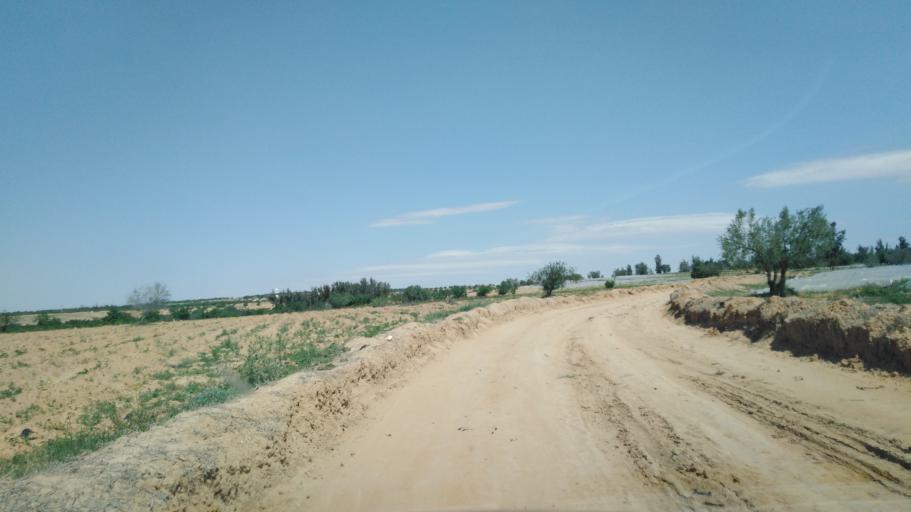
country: TN
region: Safaqis
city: Sfax
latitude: 34.7678
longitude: 10.5274
